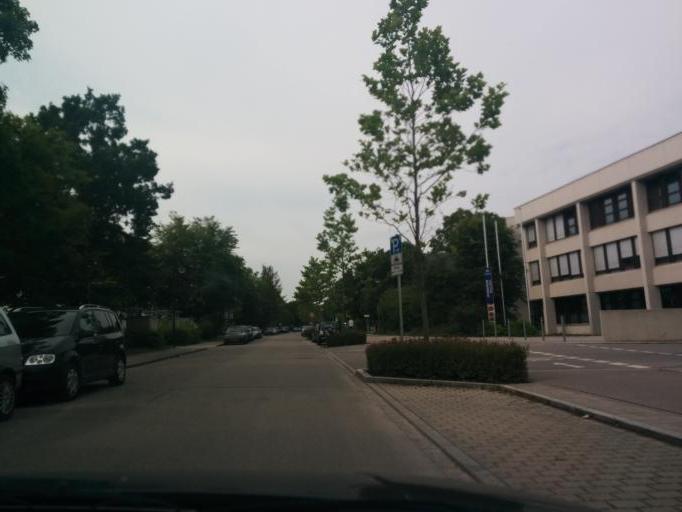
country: DE
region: Bavaria
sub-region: Upper Bavaria
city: Pullach im Isartal
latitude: 48.0667
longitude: 11.5271
